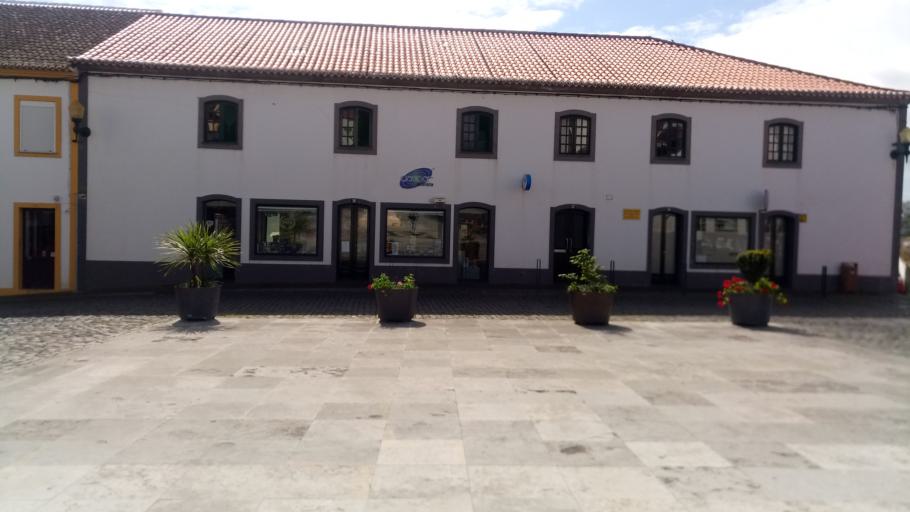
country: PT
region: Azores
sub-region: Praia da Vitoria
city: Praia da Vitoria
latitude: 38.7310
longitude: -27.0603
